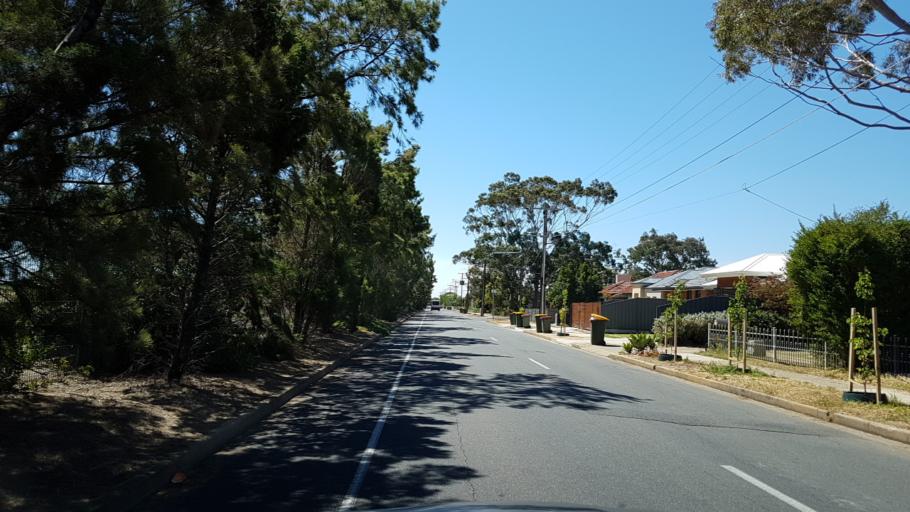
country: AU
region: South Australia
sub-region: Marion
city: Plympton Park
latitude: -34.9795
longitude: 138.5471
